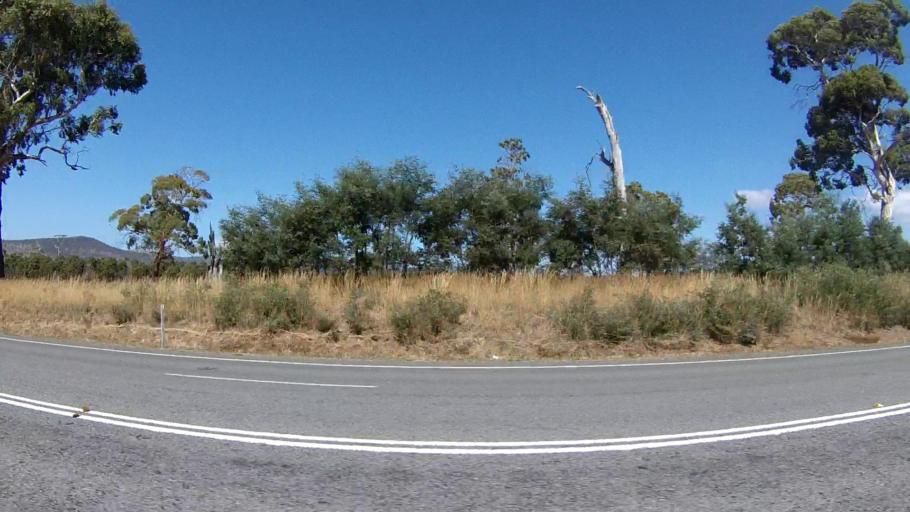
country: AU
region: Tasmania
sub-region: Sorell
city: Sorell
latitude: -42.6020
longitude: 147.7548
